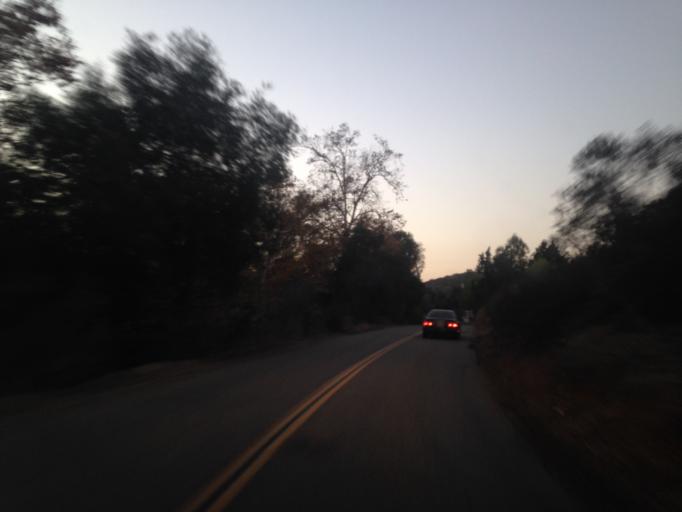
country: US
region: California
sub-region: San Diego County
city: Bonsall
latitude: 33.2595
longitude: -117.2134
